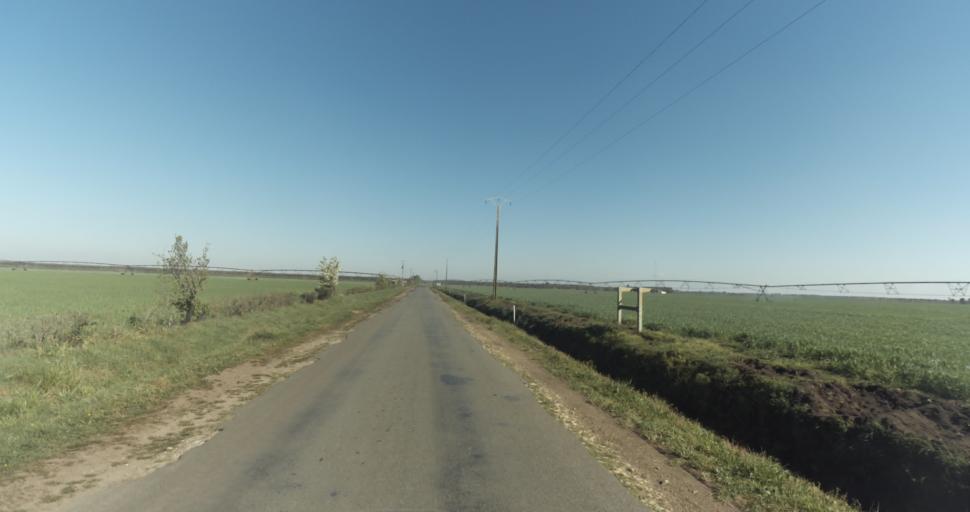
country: FR
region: Aquitaine
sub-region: Departement de la Gironde
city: Marcheprime
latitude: 44.7672
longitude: -0.8551
